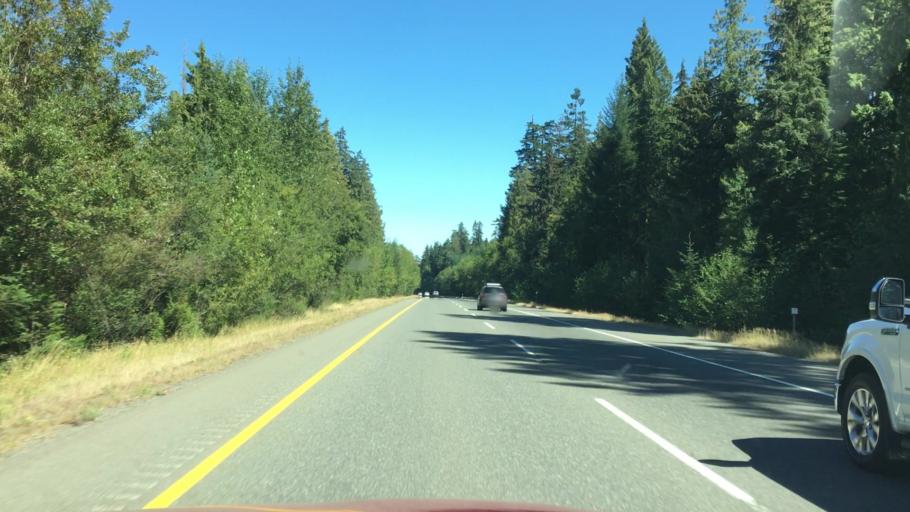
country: CA
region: British Columbia
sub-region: Regional District of Nanaimo
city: Parksville
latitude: 49.3180
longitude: -124.3926
